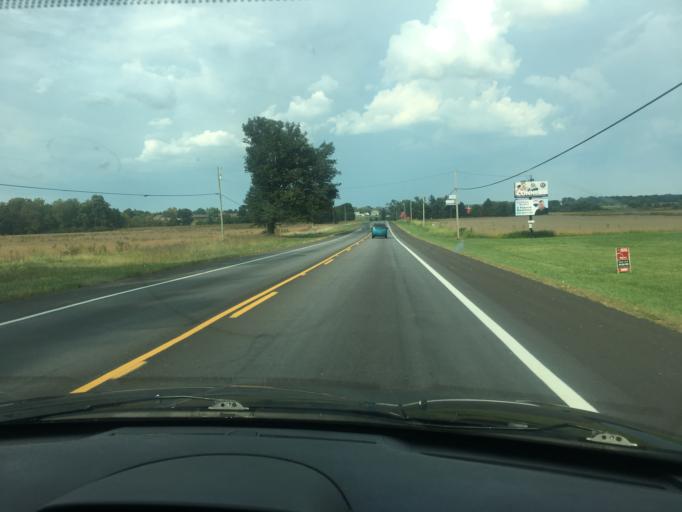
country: US
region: Ohio
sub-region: Champaign County
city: Urbana
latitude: 40.0720
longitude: -83.7694
